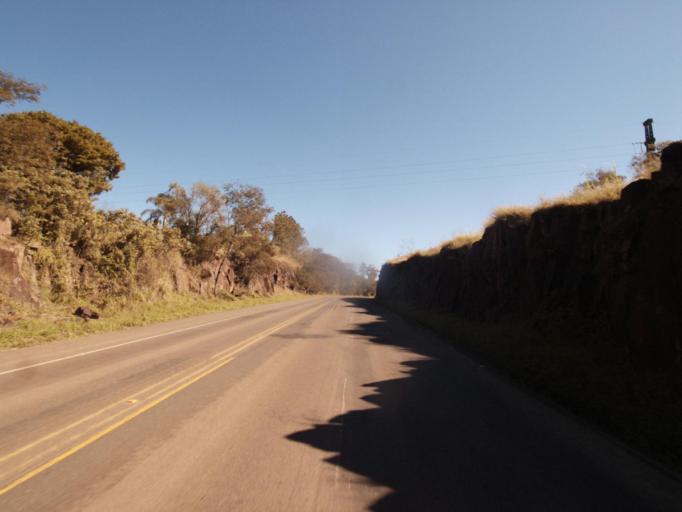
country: AR
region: Misiones
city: Bernardo de Irigoyen
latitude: -26.7658
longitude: -53.4903
